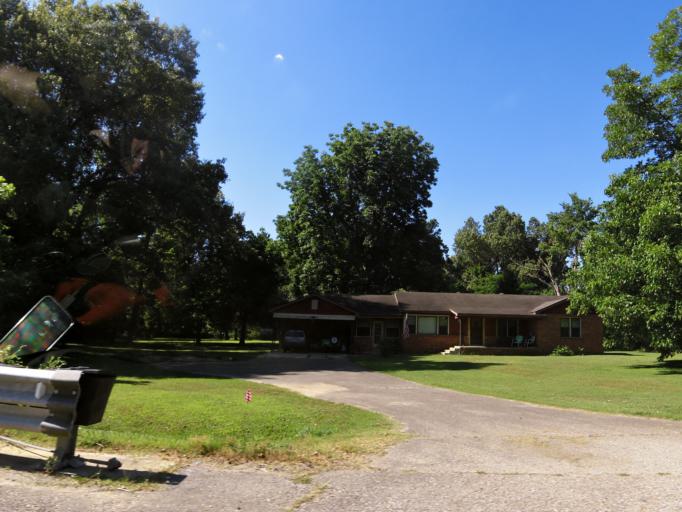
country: US
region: Arkansas
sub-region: Clay County
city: Piggott
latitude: 36.3893
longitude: -90.1973
